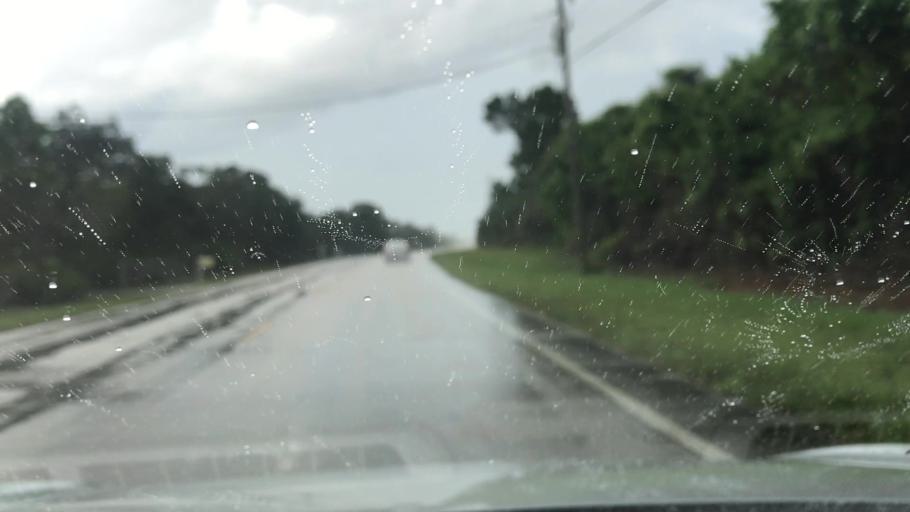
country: US
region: Florida
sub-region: Indian River County
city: Roseland
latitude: 27.8062
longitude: -80.5030
